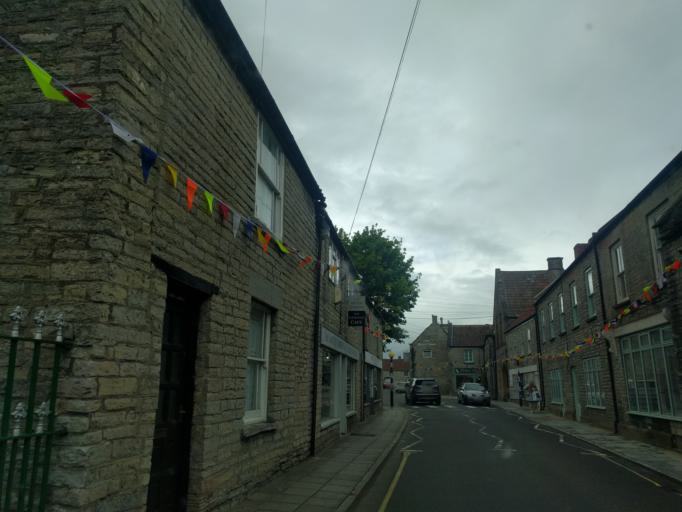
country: GB
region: England
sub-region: Somerset
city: Ilchester
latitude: 51.0537
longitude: -2.7296
